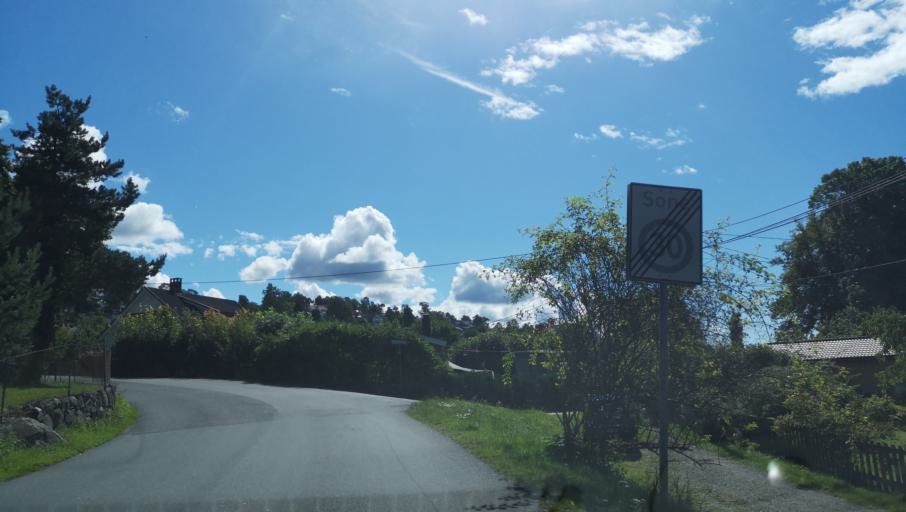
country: NO
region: Akershus
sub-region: Frogn
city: Drobak
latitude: 59.6545
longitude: 10.6358
